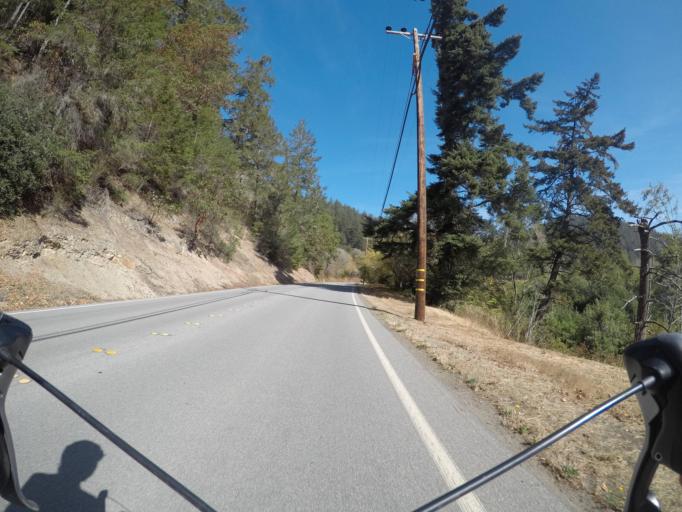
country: US
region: California
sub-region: San Mateo County
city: Portola Valley
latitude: 37.2594
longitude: -122.3393
